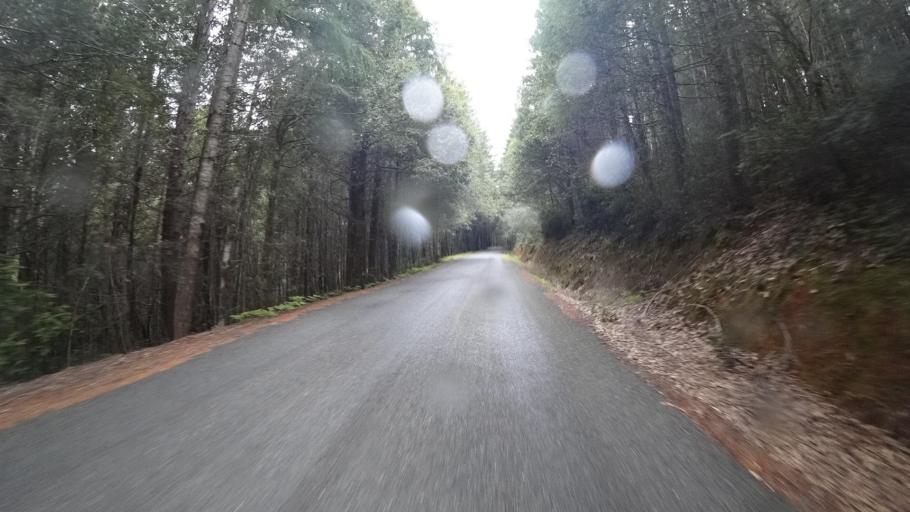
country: US
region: California
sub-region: Humboldt County
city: Willow Creek
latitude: 41.1994
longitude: -123.7672
